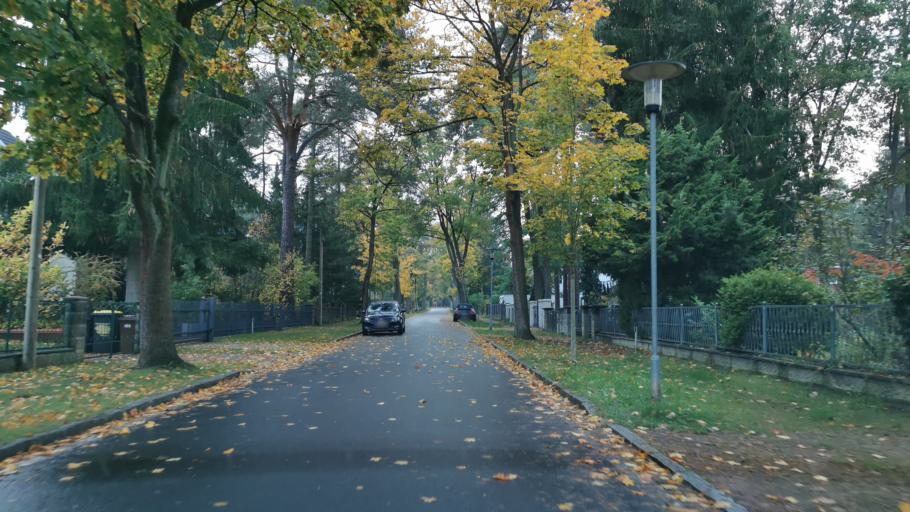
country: DE
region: Brandenburg
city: Michendorf
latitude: 52.3291
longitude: 13.0672
